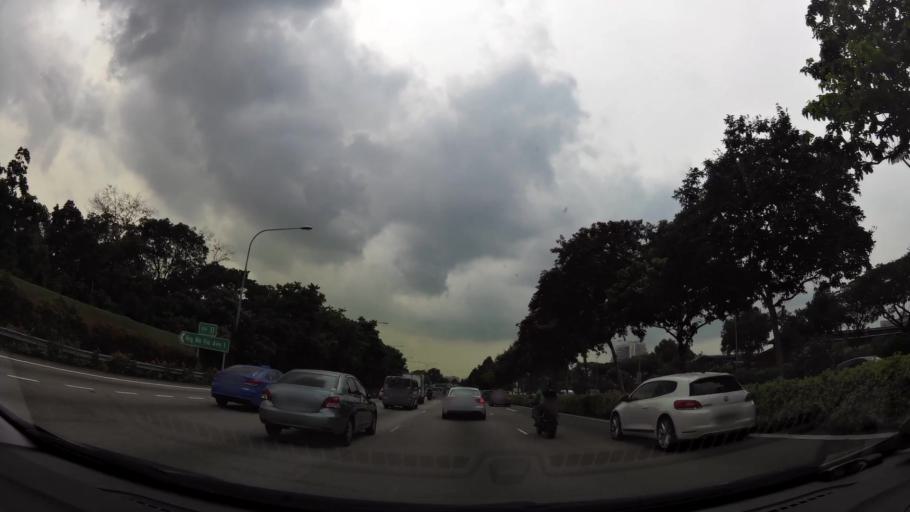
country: SG
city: Singapore
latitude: 1.3589
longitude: 103.8578
